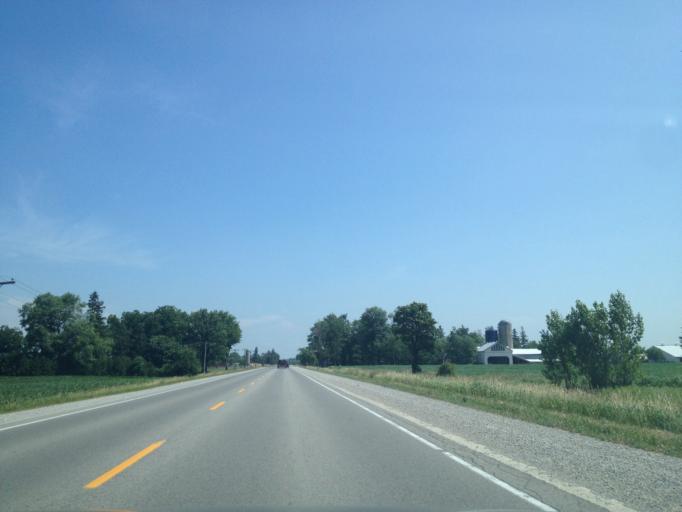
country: CA
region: Ontario
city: Huron East
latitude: 43.4481
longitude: -81.2148
